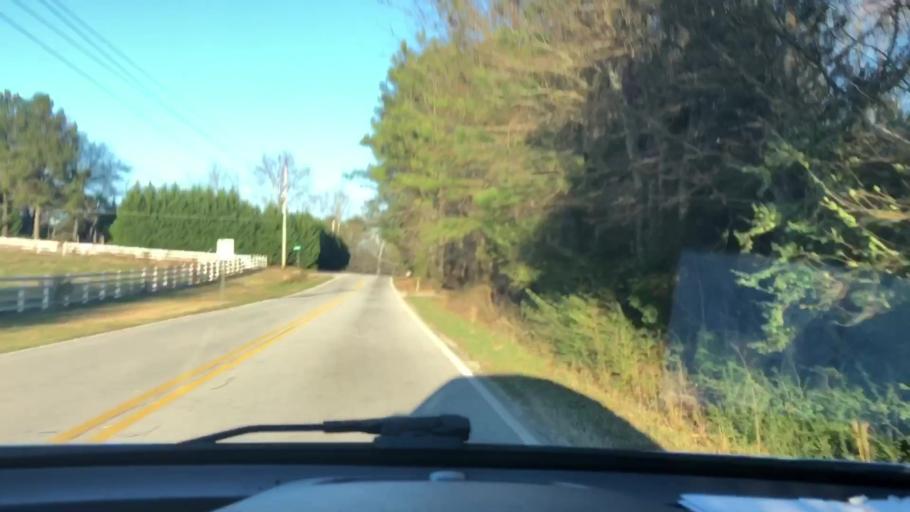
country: US
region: Georgia
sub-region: Rockdale County
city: Lakeview Estates
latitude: 33.7465
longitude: -84.0328
